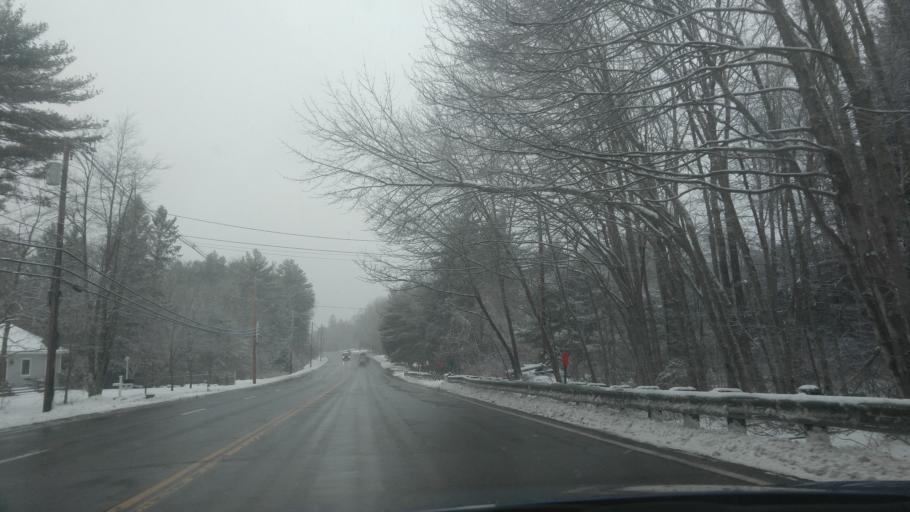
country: US
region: Rhode Island
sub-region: Providence County
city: Foster
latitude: 41.8260
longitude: -71.6799
